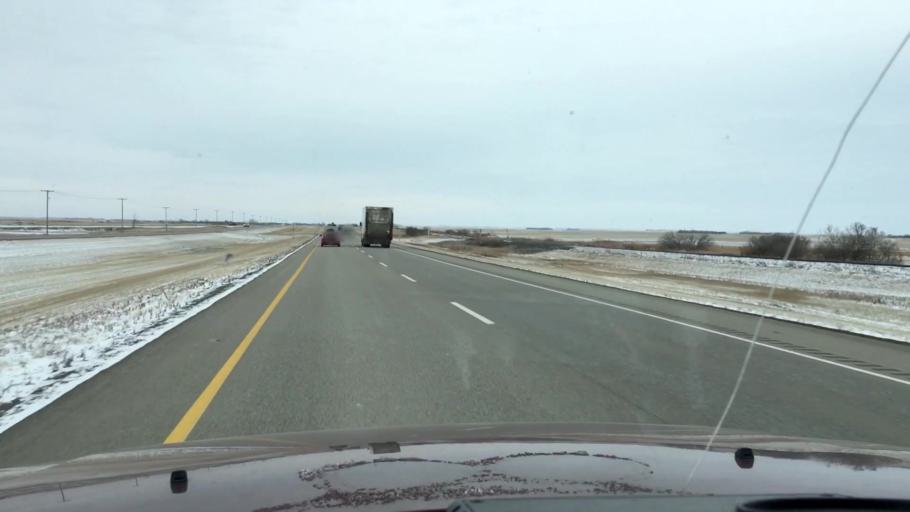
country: CA
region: Saskatchewan
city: Watrous
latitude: 51.1849
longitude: -105.9434
